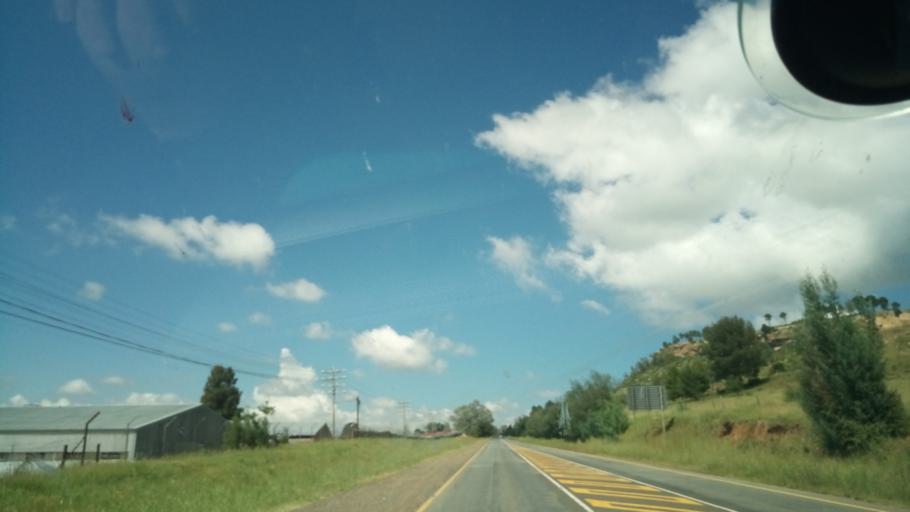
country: ZA
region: Orange Free State
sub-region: Thabo Mofutsanyana District Municipality
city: Ficksburg
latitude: -28.8549
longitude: 27.8787
